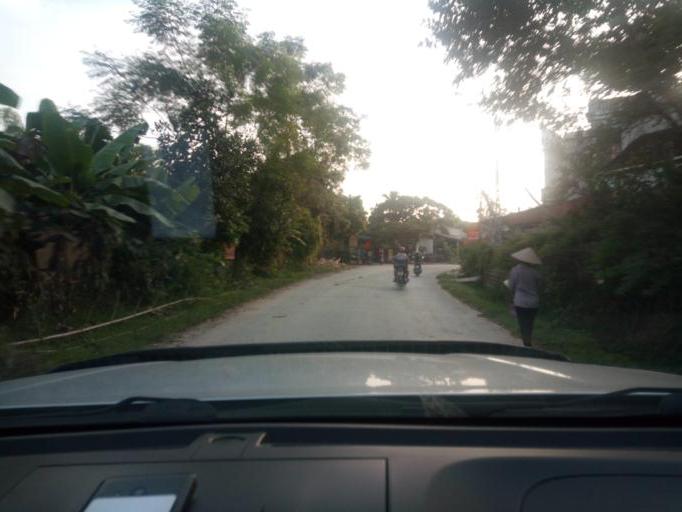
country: VN
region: Yen Bai
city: Co Phuc
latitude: 21.8770
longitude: 104.6623
